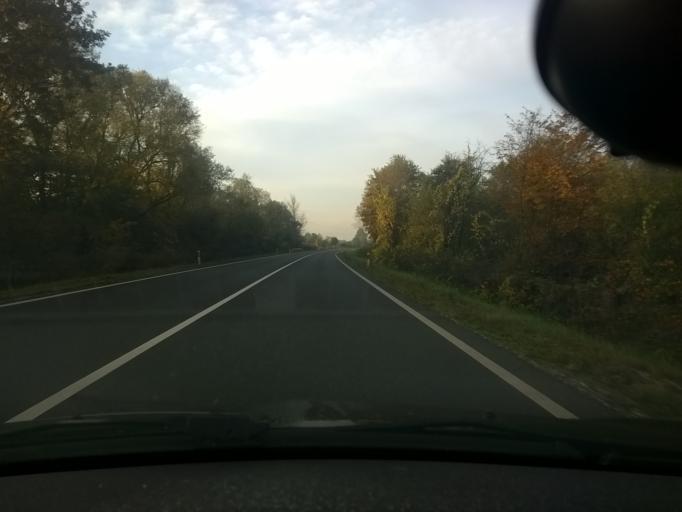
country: HR
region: Zagrebacka
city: Jakovlje
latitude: 45.9686
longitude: 15.8473
